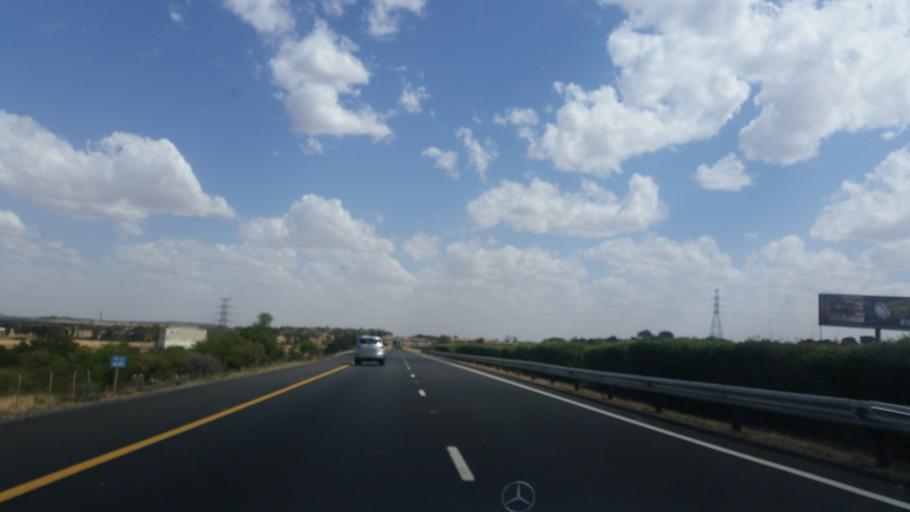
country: ZA
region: Orange Free State
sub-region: Mangaung Metropolitan Municipality
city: Bloemfontein
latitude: -29.0832
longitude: 26.1762
